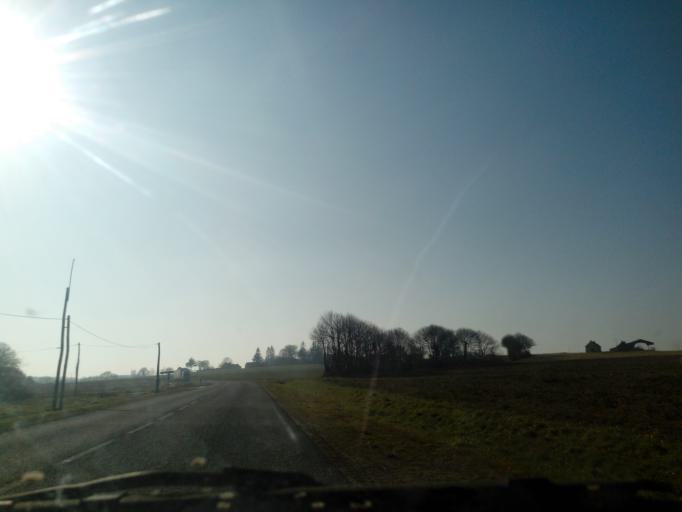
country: FR
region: Brittany
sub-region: Departement du Morbihan
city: Meneac
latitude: 48.1661
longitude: -2.4410
